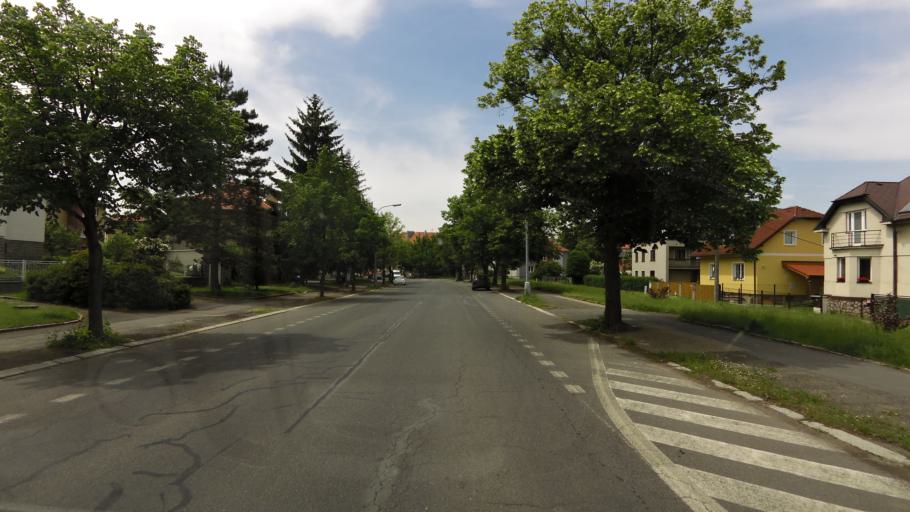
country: CZ
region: Plzensky
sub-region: Okres Rokycany
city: Rokycany
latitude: 49.7439
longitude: 13.6062
